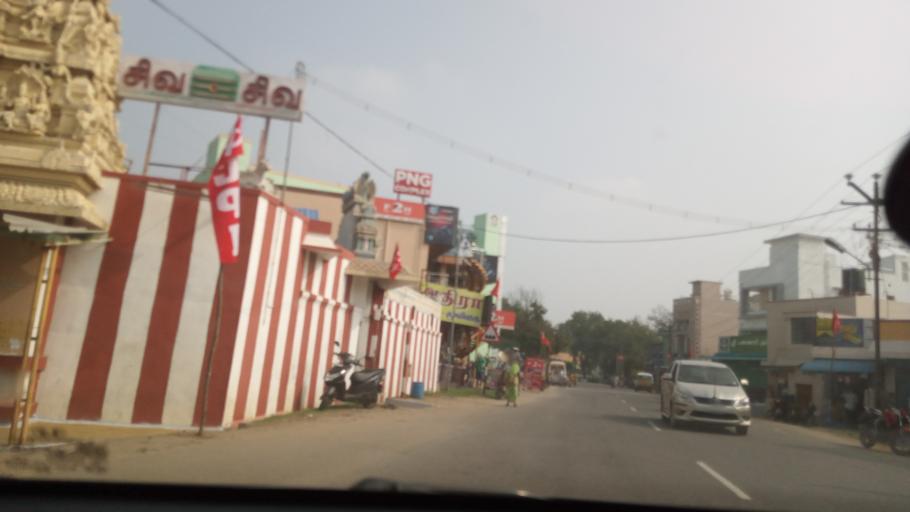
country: IN
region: Tamil Nadu
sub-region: Erode
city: Punjai Puliyampatti
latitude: 11.3537
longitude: 77.1686
